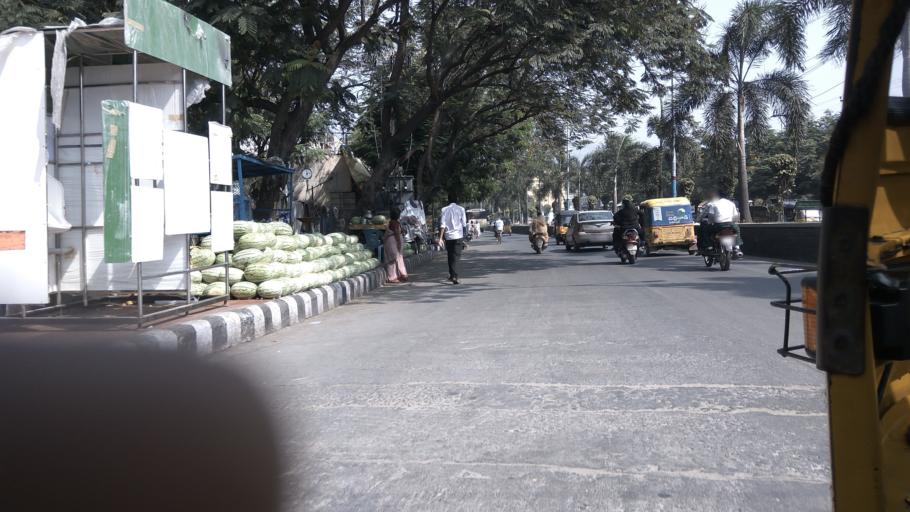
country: IN
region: Andhra Pradesh
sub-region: Chittoor
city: Tirupati
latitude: 13.6333
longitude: 79.4133
